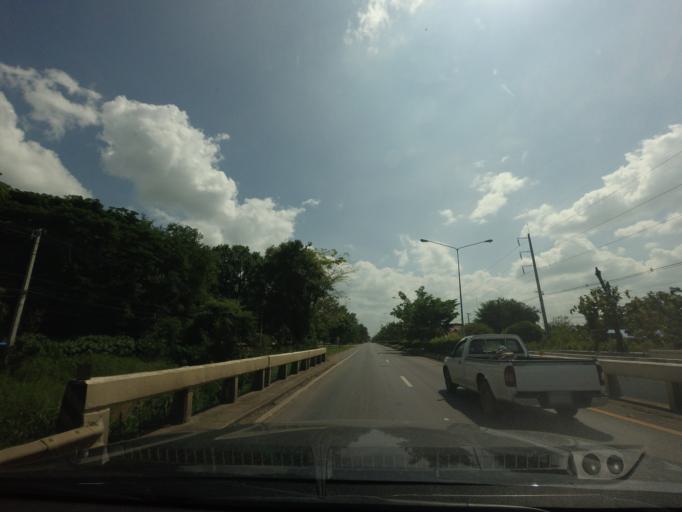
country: TH
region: Phetchabun
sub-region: Amphoe Bueng Sam Phan
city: Bueng Sam Phan
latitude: 15.8630
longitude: 101.0123
